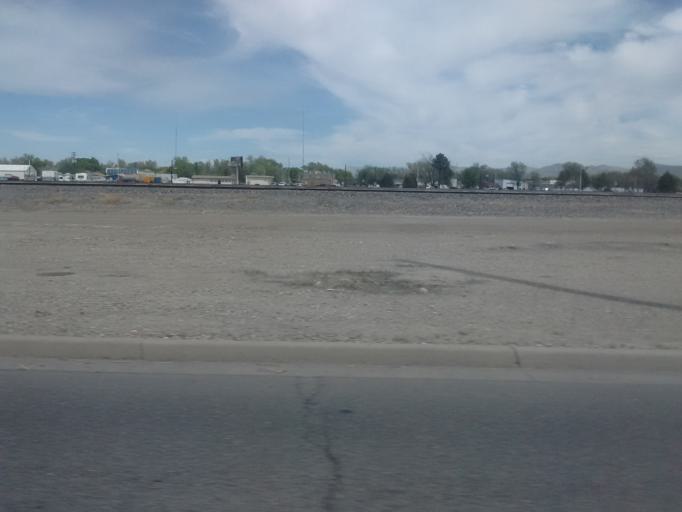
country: US
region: Colorado
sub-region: Mesa County
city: Grand Junction
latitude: 39.0629
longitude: -108.5491
